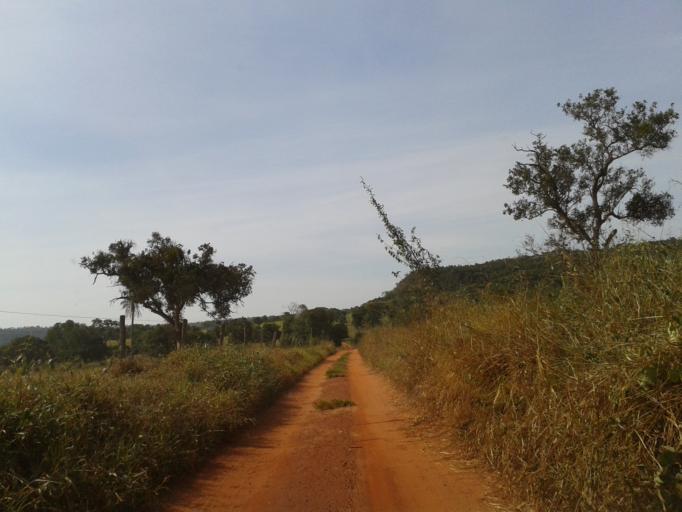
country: BR
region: Minas Gerais
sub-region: Campina Verde
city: Campina Verde
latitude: -19.5196
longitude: -49.5921
